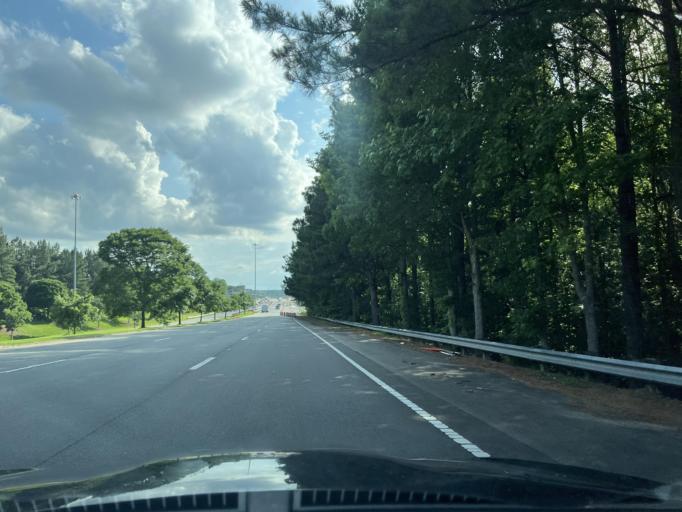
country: US
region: North Carolina
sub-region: Wake County
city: Morrisville
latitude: 35.8648
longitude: -78.8080
